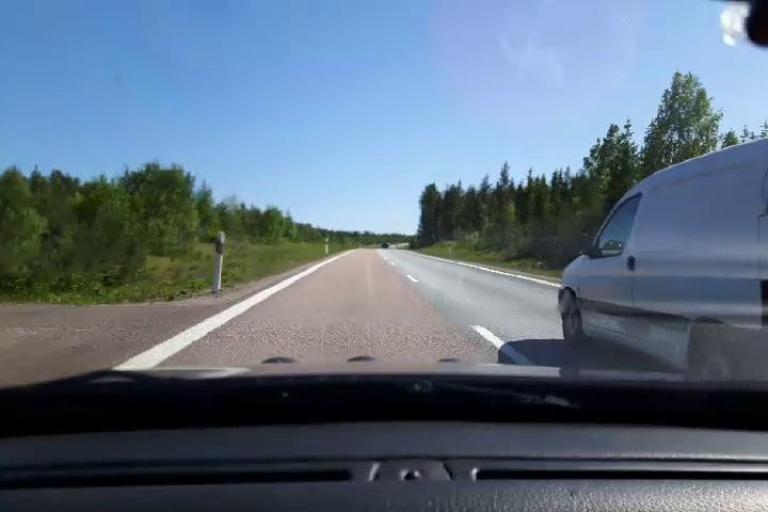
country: SE
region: Gaevleborg
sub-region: Soderhamns Kommun
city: Soderhamn
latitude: 61.4770
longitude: 16.9882
